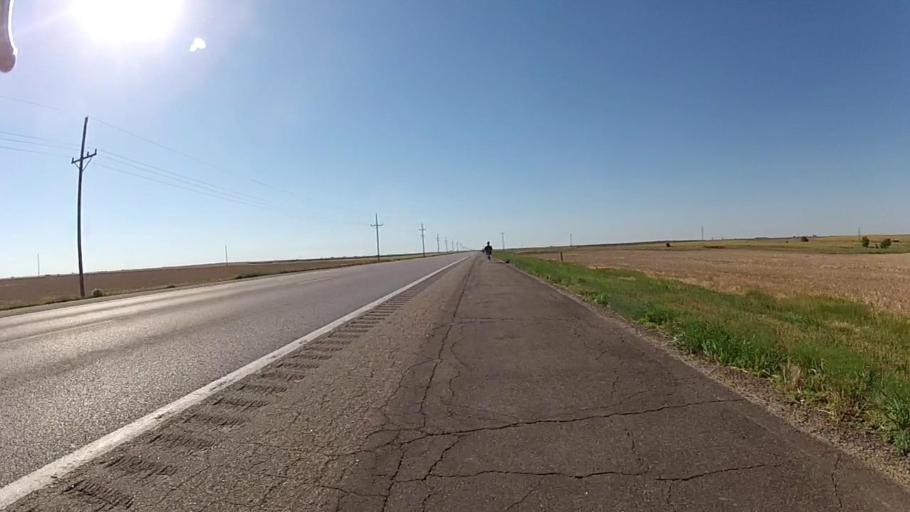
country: US
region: Kansas
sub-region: Ford County
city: Dodge City
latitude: 37.6074
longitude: -99.7100
